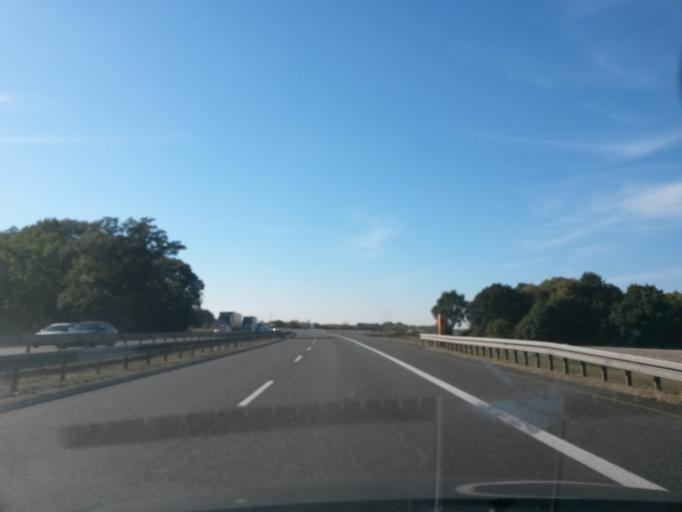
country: PL
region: Opole Voivodeship
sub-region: Powiat brzeski
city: Grodkow
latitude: 50.7687
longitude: 17.4027
